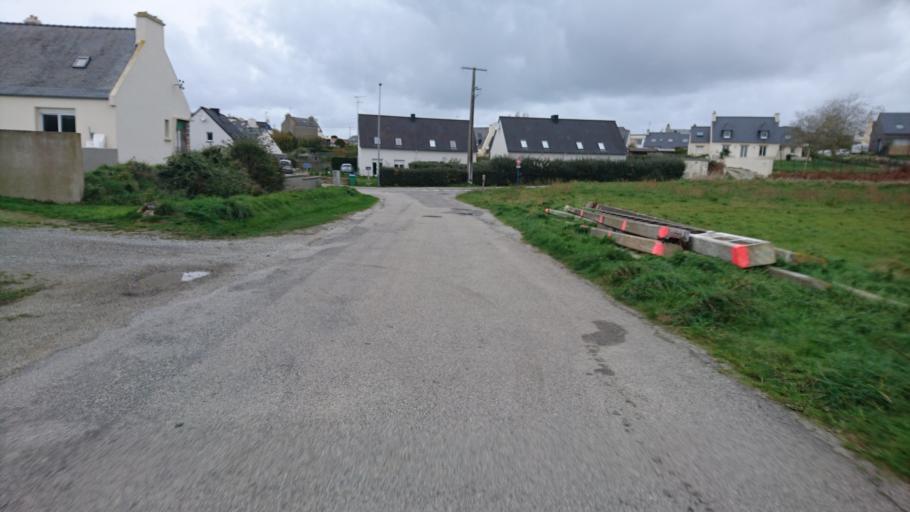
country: FR
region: Brittany
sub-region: Departement du Finistere
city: Lampaul-Plouarzel
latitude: 48.4459
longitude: -4.7666
